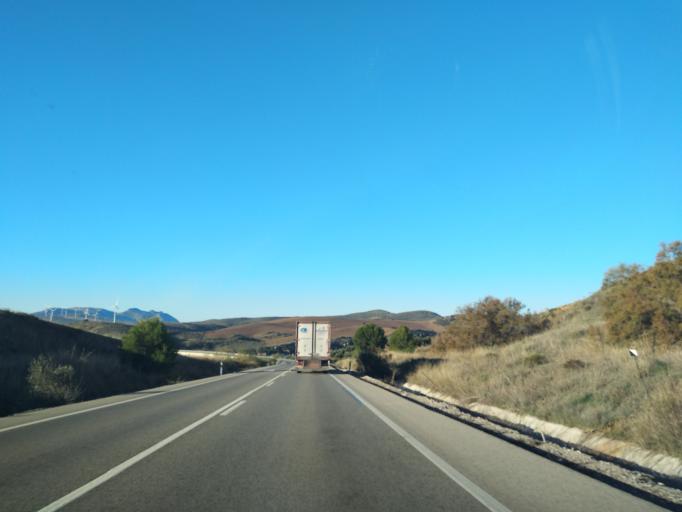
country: ES
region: Andalusia
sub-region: Provincia de Malaga
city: Teba
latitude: 36.9639
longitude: -4.8526
